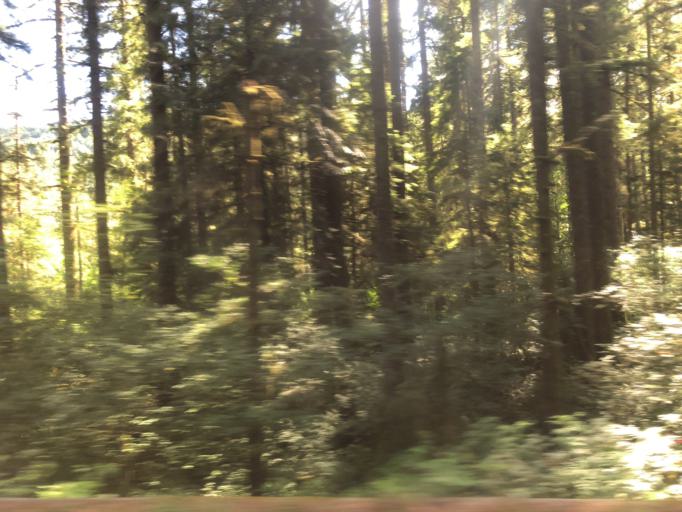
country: US
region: Oregon
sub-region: Clackamas County
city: Sandy
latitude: 45.4257
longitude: -122.2245
